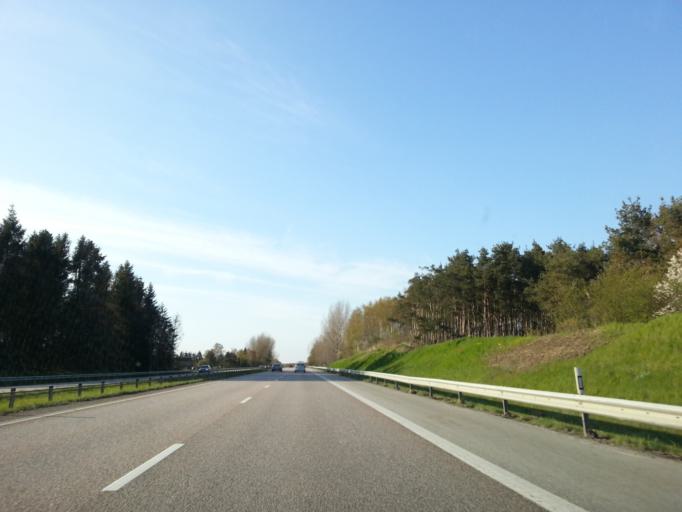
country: SE
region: Skane
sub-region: Kavlinge Kommun
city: Hofterup
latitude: 55.7884
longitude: 12.9664
